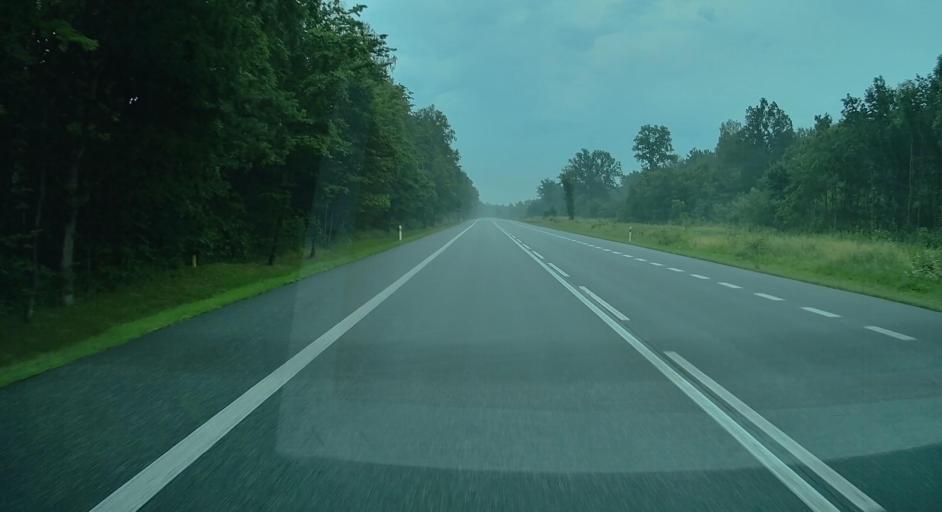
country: PL
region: Masovian Voivodeship
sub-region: Powiat siedlecki
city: Zbuczyn
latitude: 52.0831
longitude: 22.4673
